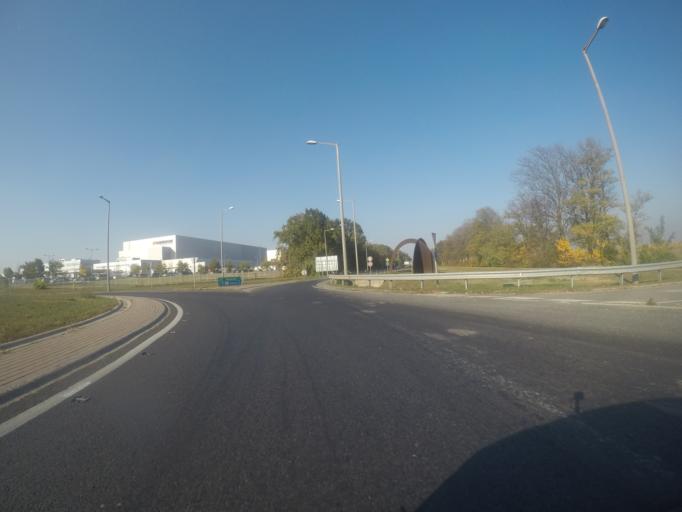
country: HU
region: Fejer
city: Racalmas
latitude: 46.9988
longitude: 18.9302
